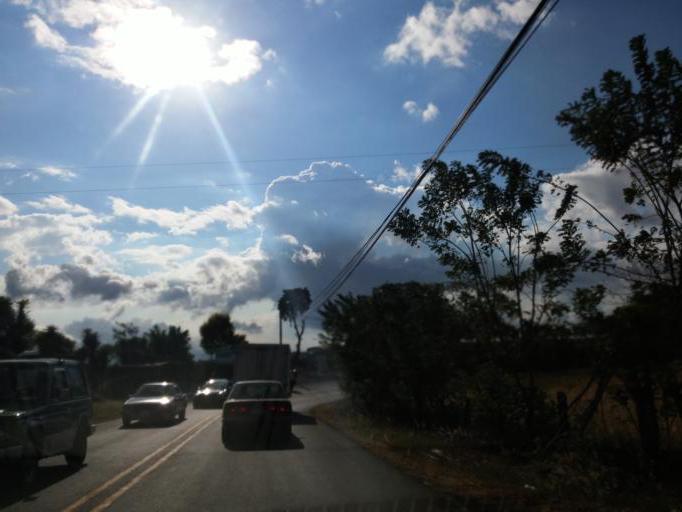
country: CR
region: San Jose
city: San Ignacio
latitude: 9.7951
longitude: -84.1422
